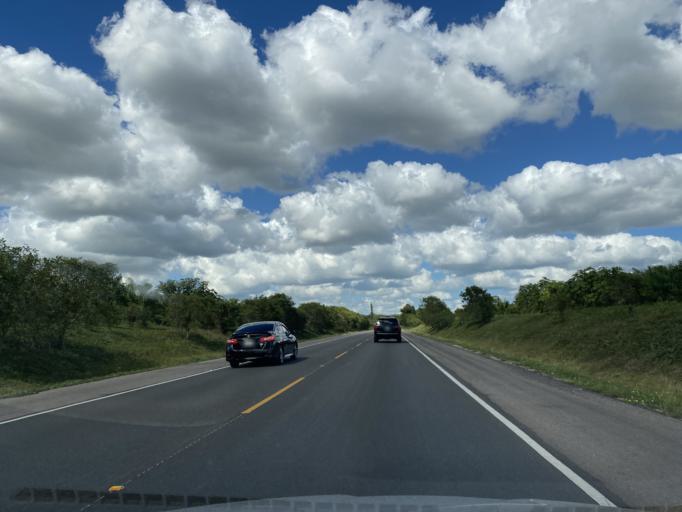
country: DO
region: Monte Plata
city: Monte Plata
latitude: 18.7387
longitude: -69.7633
